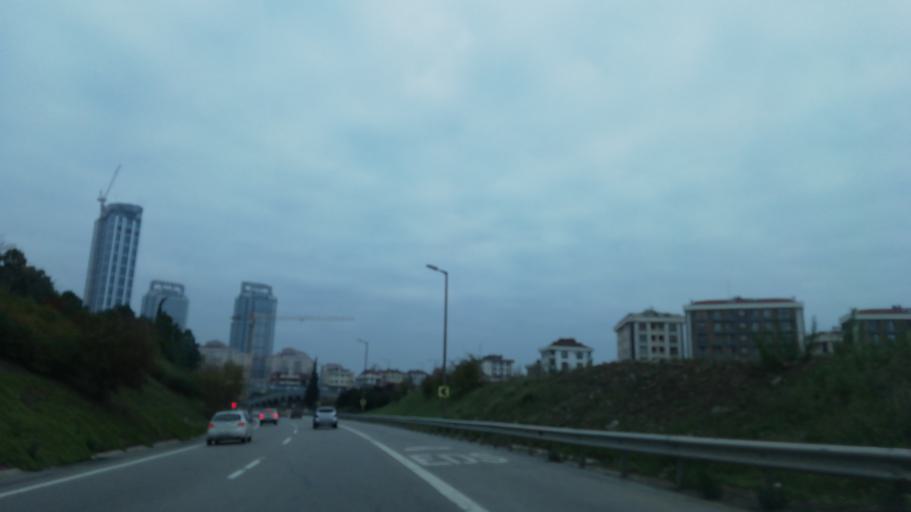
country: TR
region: Istanbul
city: UEskuedar
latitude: 41.0079
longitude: 29.0621
